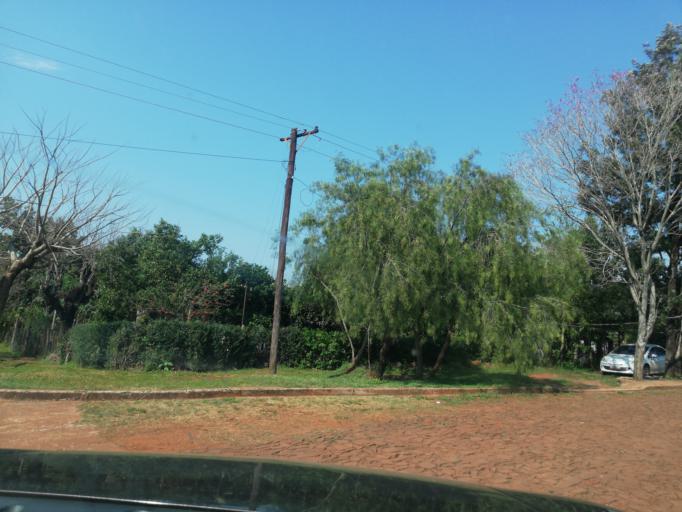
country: AR
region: Misiones
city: Bonpland
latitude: -27.4859
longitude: -55.4777
